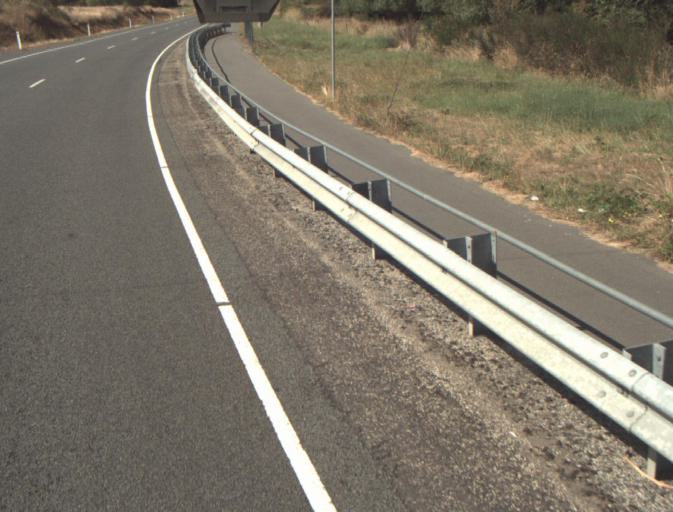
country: AU
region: Tasmania
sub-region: Launceston
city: Newstead
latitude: -41.4263
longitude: 147.1861
